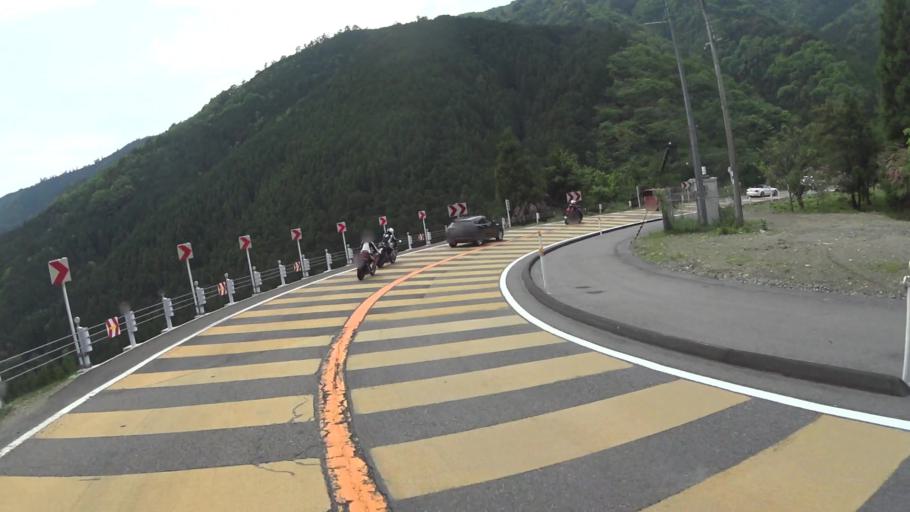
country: JP
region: Shiga Prefecture
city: Kitahama
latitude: 35.1770
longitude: 135.8588
